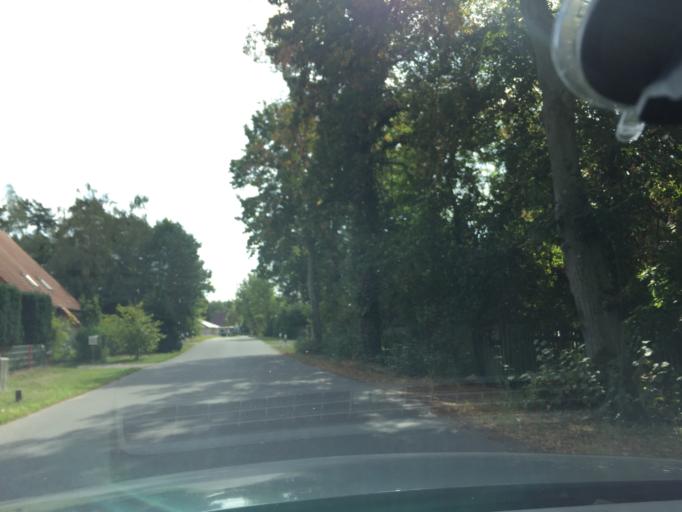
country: DE
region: Brandenburg
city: Grunheide
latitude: 52.3808
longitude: 13.7959
